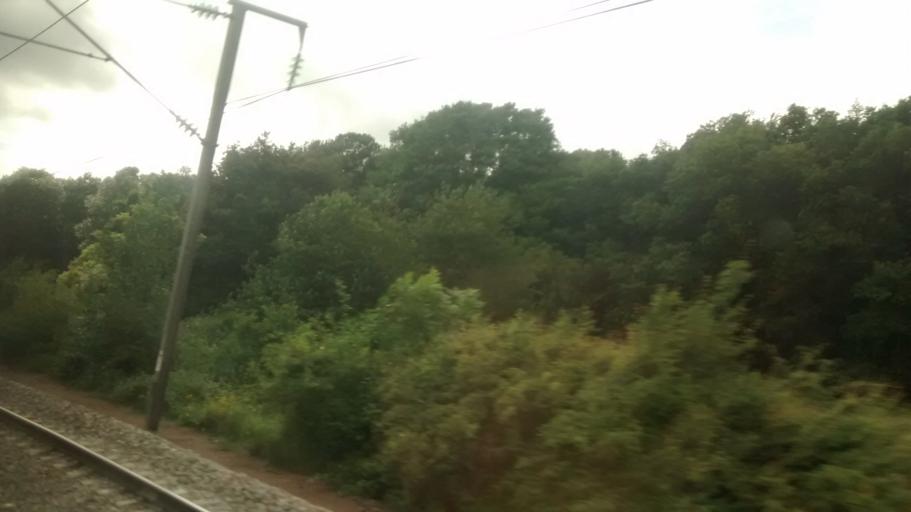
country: FR
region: Centre
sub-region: Departement d'Eure-et-Loir
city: Aunay-sous-Auneau
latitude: 48.4661
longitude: 1.8253
